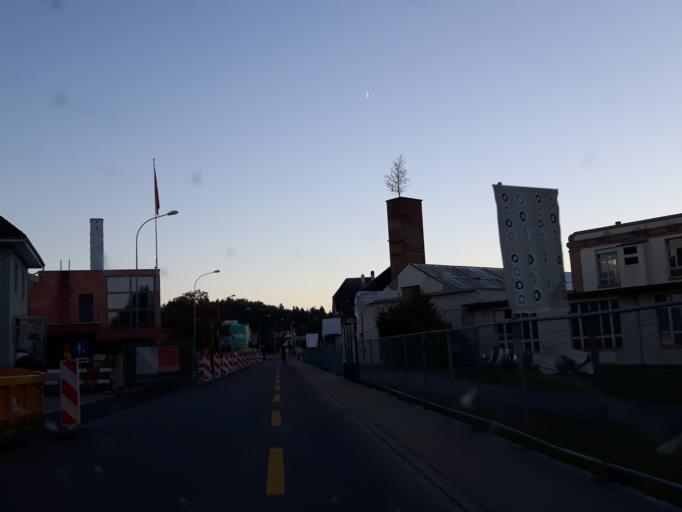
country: CH
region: Bern
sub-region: Oberaargau
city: Lotzwil
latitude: 47.2046
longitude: 7.7826
